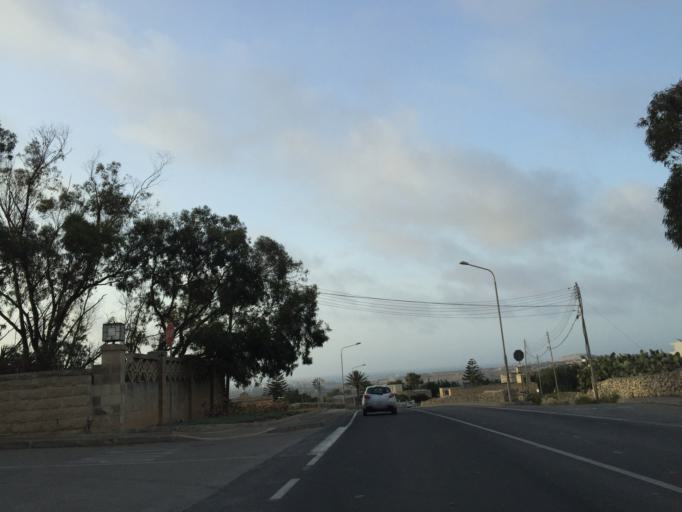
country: MT
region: Il-Mosta
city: Mosta
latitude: 35.9143
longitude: 14.4155
